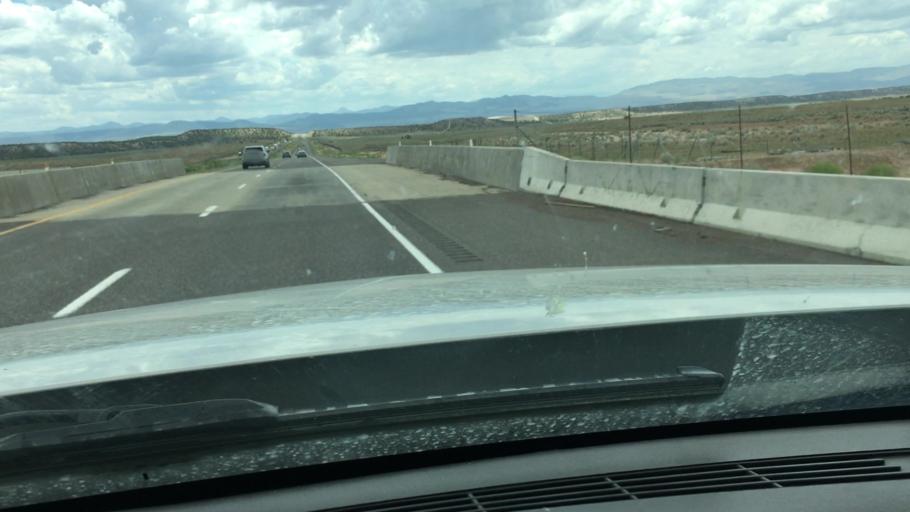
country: US
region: Utah
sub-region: Beaver County
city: Beaver
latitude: 38.3598
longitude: -112.6616
